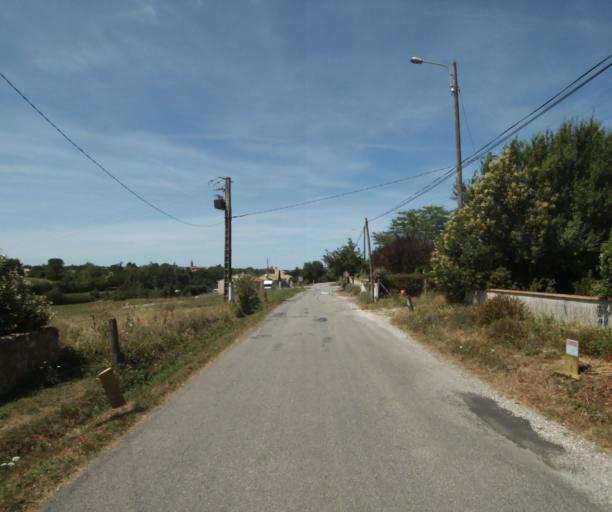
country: FR
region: Midi-Pyrenees
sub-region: Departement de la Haute-Garonne
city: Revel
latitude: 43.4879
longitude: 2.0257
